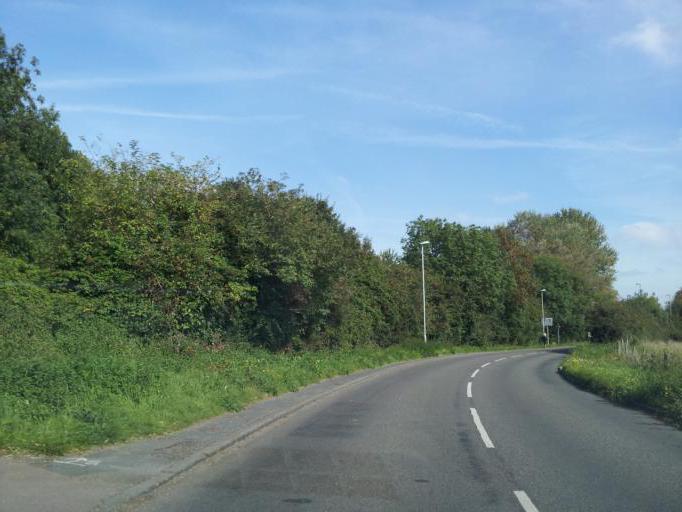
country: GB
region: England
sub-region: Cambridgeshire
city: Girton
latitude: 52.2650
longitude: 0.0750
